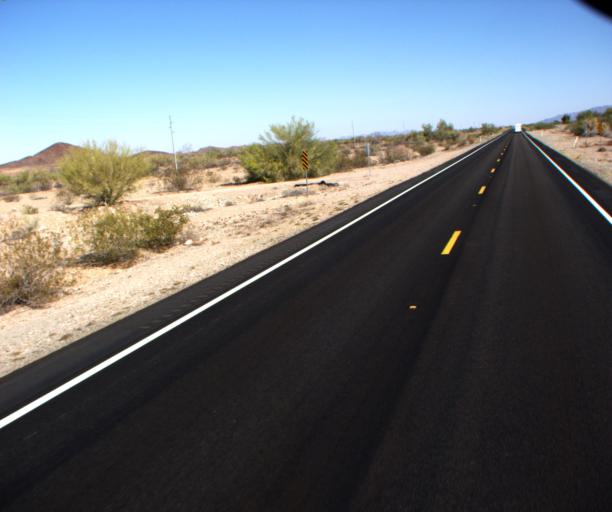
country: US
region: Arizona
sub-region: Yuma County
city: Wellton
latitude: 32.9687
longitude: -114.2911
